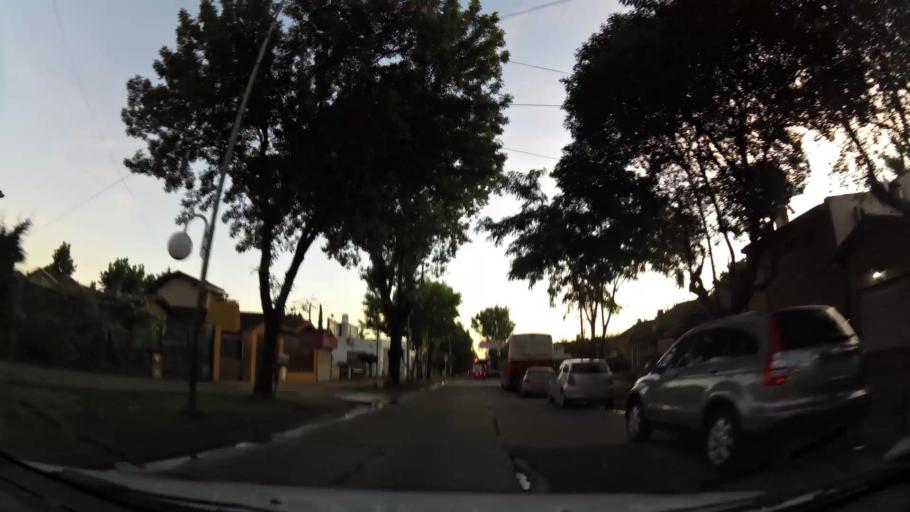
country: AR
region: Buenos Aires
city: Ituzaingo
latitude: -34.6559
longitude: -58.6435
